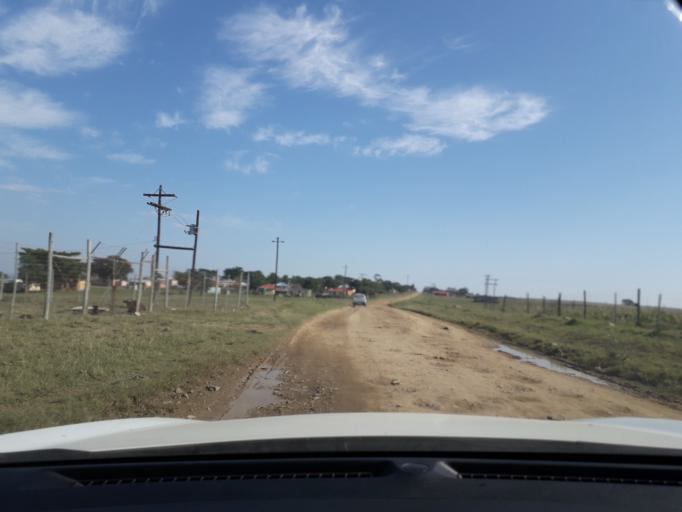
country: ZA
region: Eastern Cape
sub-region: Buffalo City Metropolitan Municipality
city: Bhisho
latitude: -32.9714
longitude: 27.3180
